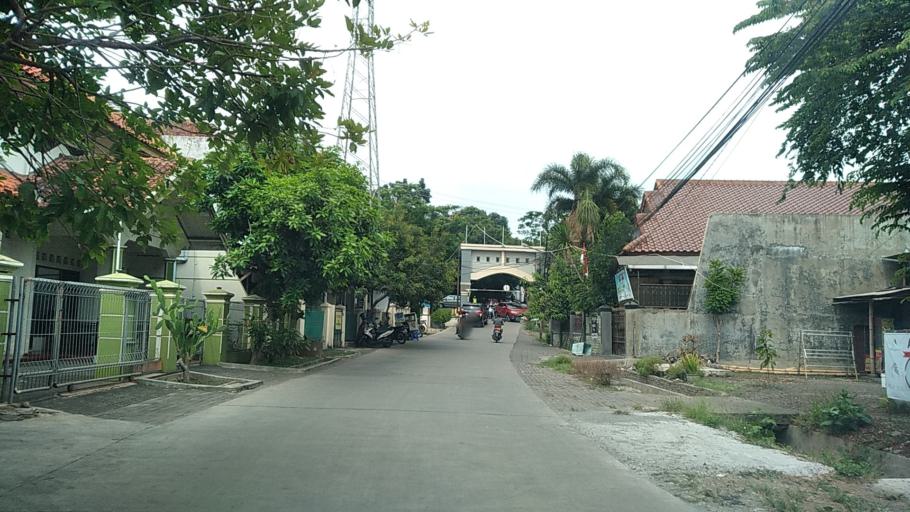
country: ID
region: Central Java
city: Semarang
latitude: -7.0577
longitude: 110.4333
